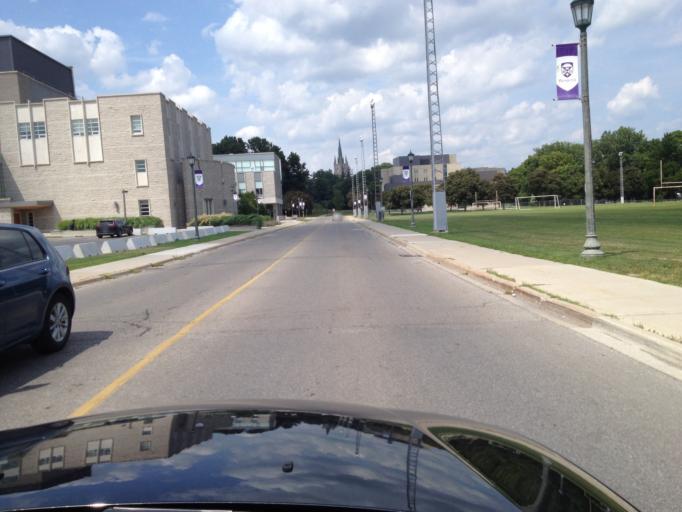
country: CA
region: Ontario
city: London
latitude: 43.0043
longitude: -81.2725
